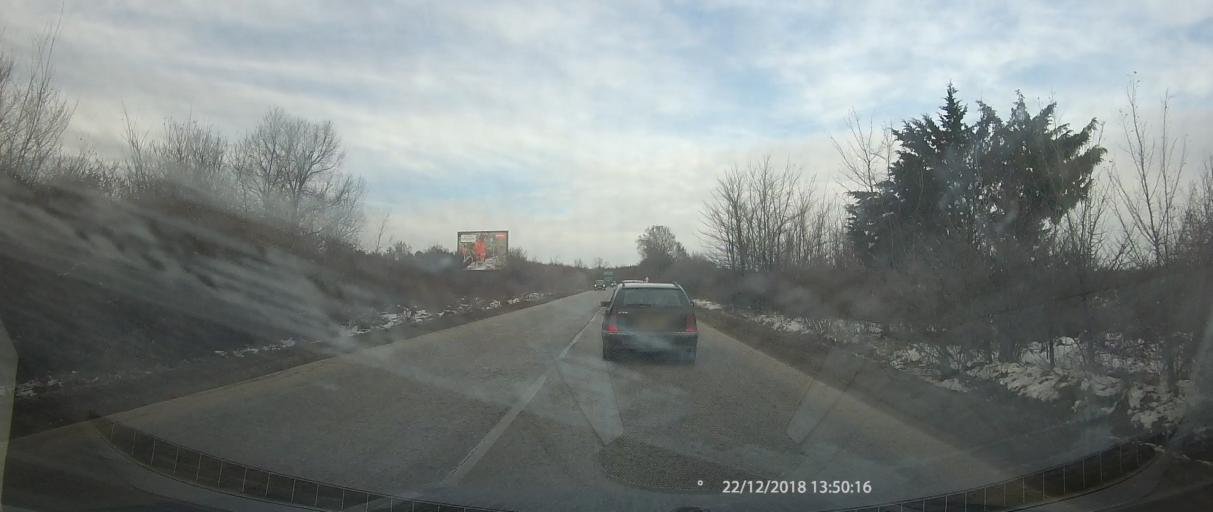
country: BG
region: Lovech
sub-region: Obshtina Lukovit
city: Lukovit
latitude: 43.2763
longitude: 24.2023
